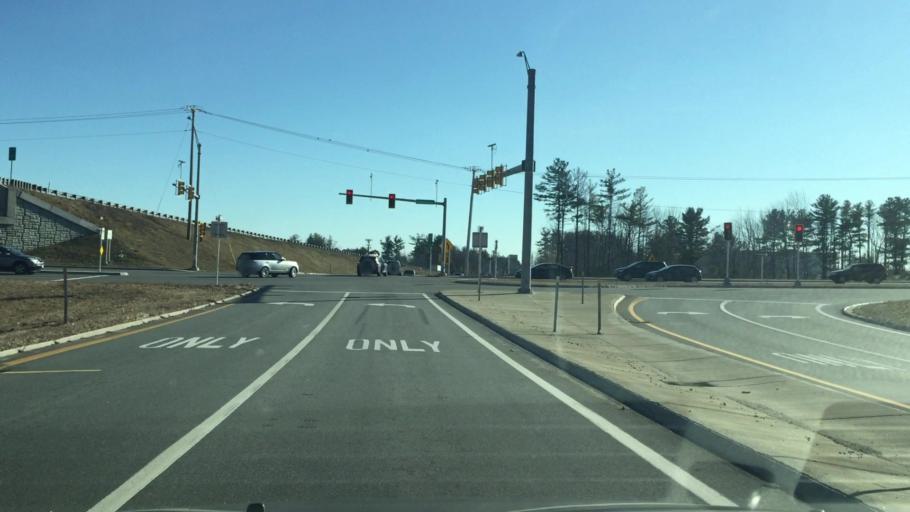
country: US
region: New Hampshire
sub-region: Rockingham County
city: Salem
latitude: 42.7775
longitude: -71.2459
